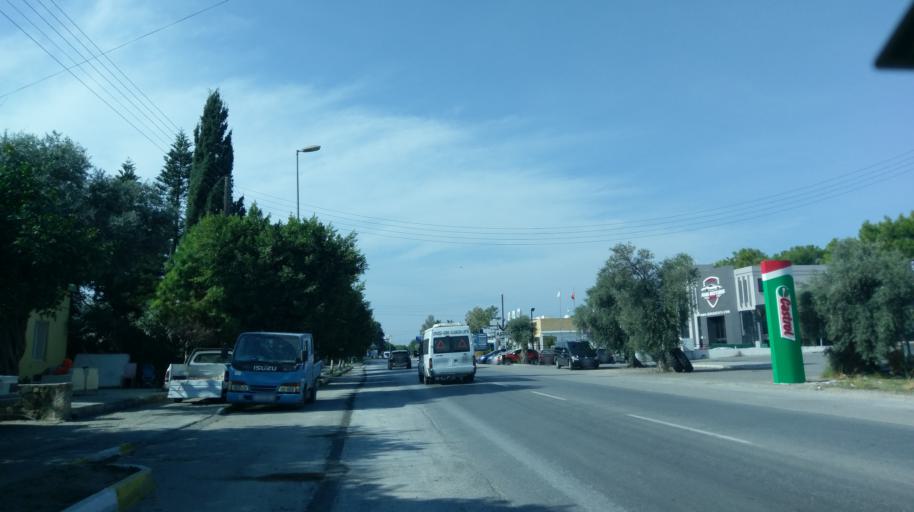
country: CY
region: Keryneia
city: Kyrenia
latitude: 35.3399
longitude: 33.2936
